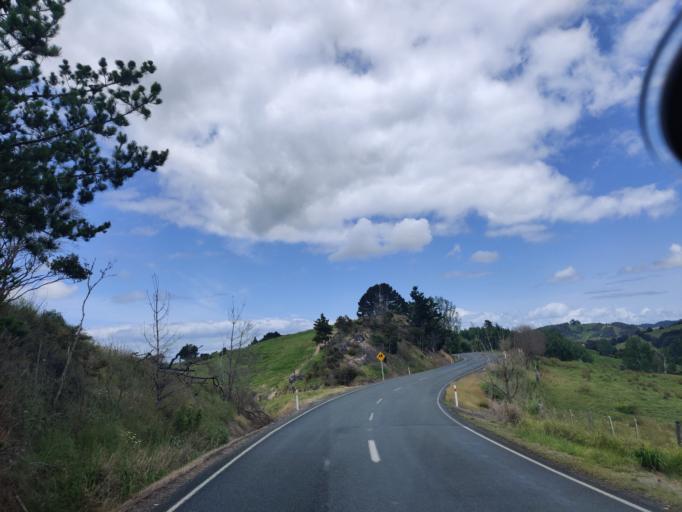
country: NZ
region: Northland
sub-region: Far North District
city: Kaitaia
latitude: -35.2783
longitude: 173.4839
